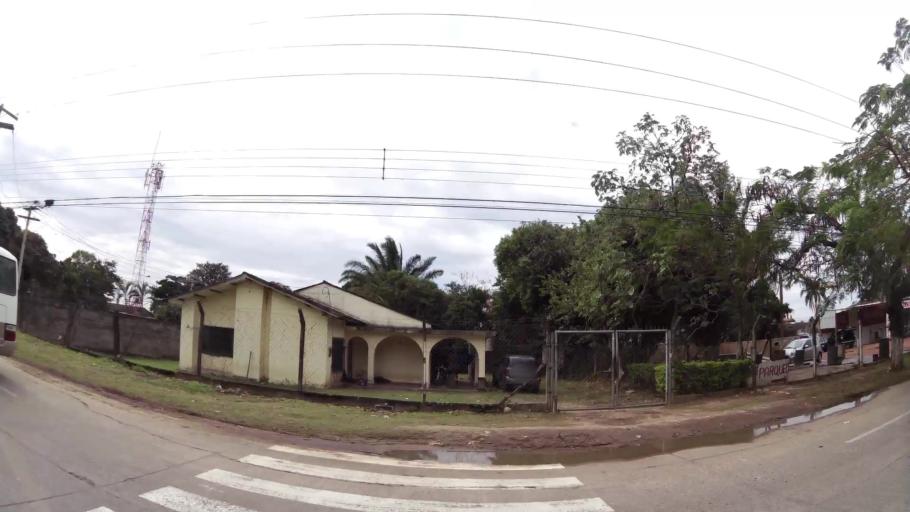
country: BO
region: Santa Cruz
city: Santa Cruz de la Sierra
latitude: -17.7580
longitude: -63.1907
